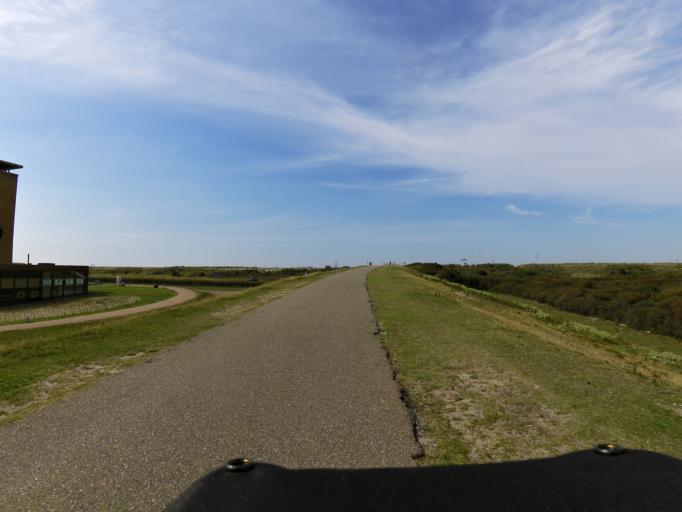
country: NL
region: Zeeland
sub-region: Schouwen-Duiveland
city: Scharendijke
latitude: 51.7585
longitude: 3.8503
